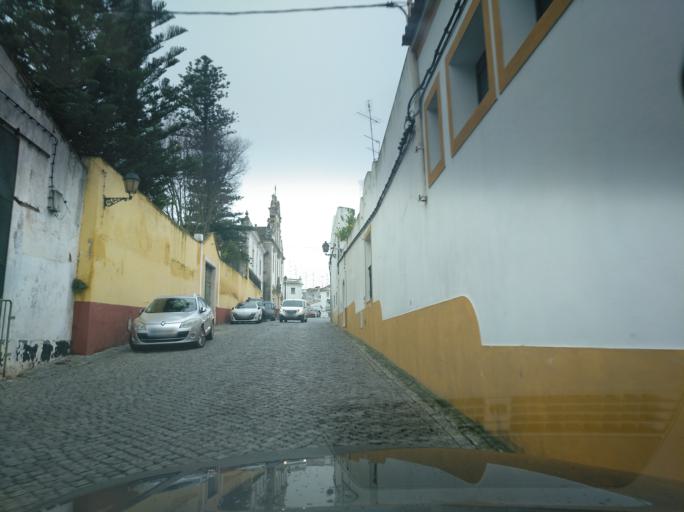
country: PT
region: Portalegre
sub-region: Elvas
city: Elvas
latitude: 38.8801
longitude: -7.1599
